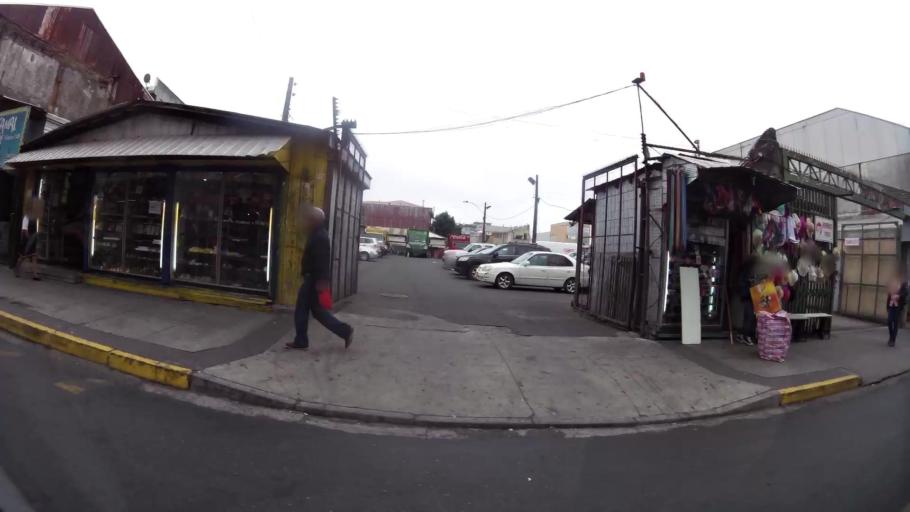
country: CL
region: Biobio
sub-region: Provincia de Concepcion
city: Concepcion
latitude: -36.8251
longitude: -73.0501
